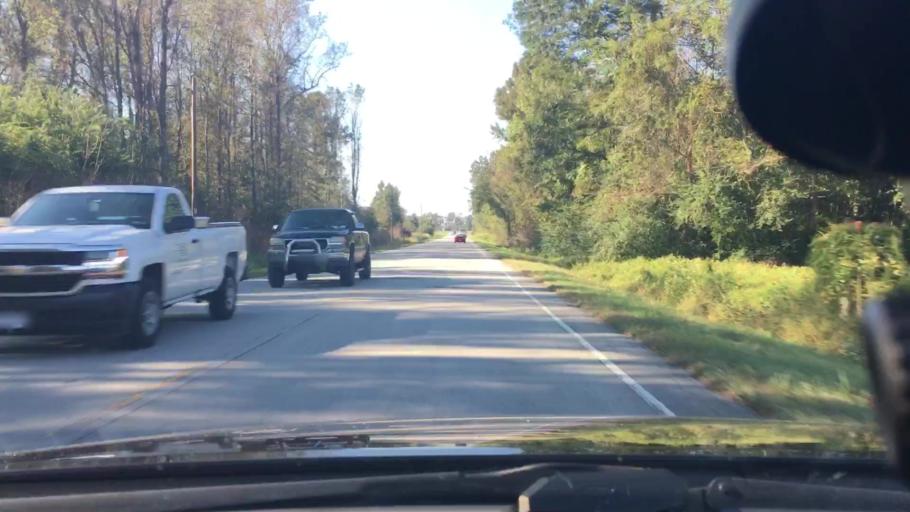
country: US
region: North Carolina
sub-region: Craven County
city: Vanceboro
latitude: 35.3682
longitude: -77.2045
